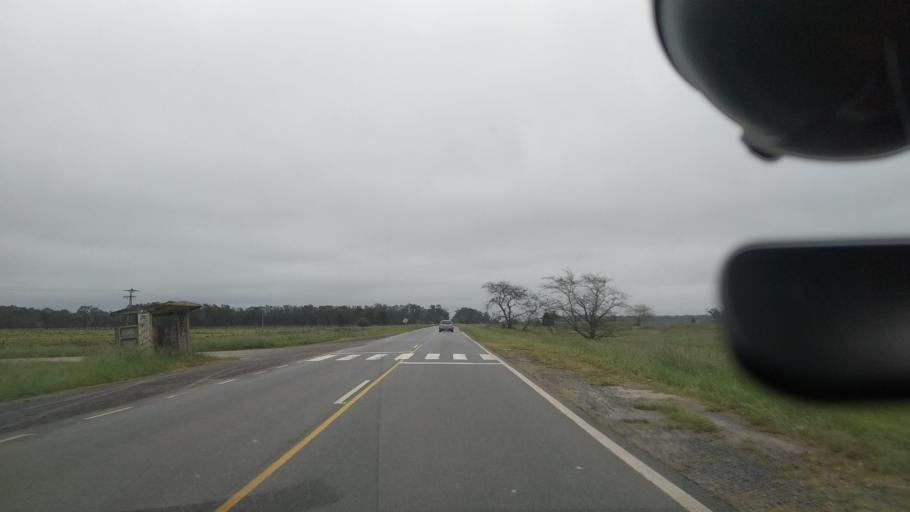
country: AR
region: Buenos Aires
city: Veronica
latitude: -35.3255
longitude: -57.4706
